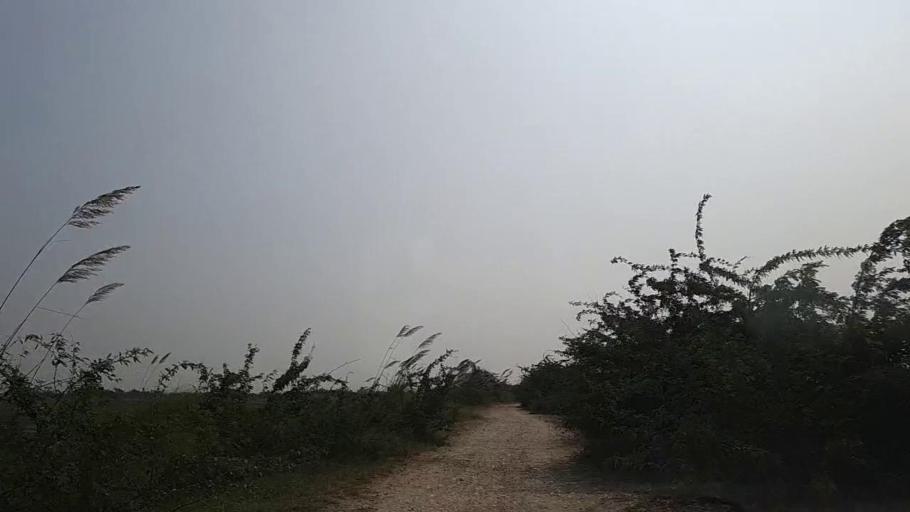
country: PK
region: Sindh
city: Mirpur Sakro
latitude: 24.5982
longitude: 67.7161
